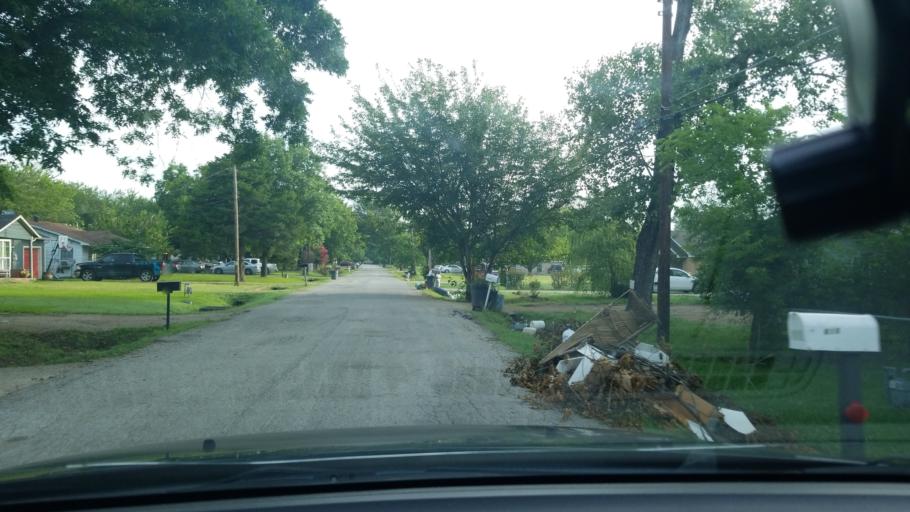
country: US
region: Texas
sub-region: Dallas County
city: Balch Springs
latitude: 32.7595
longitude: -96.6409
